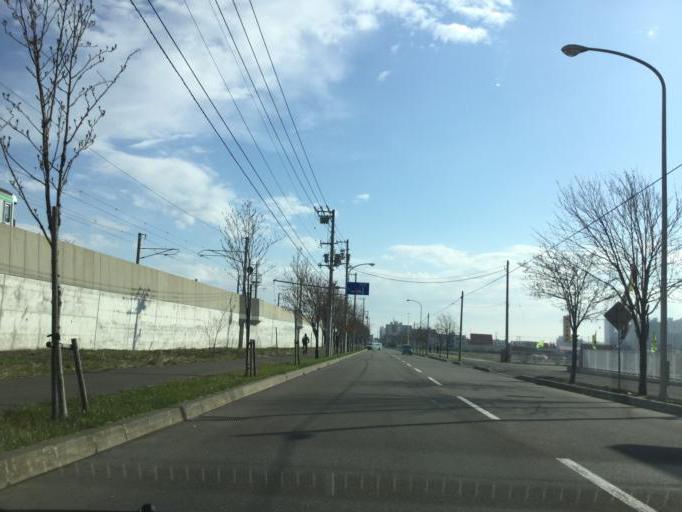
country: JP
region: Hokkaido
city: Ebetsu
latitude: 43.0865
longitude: 141.5217
